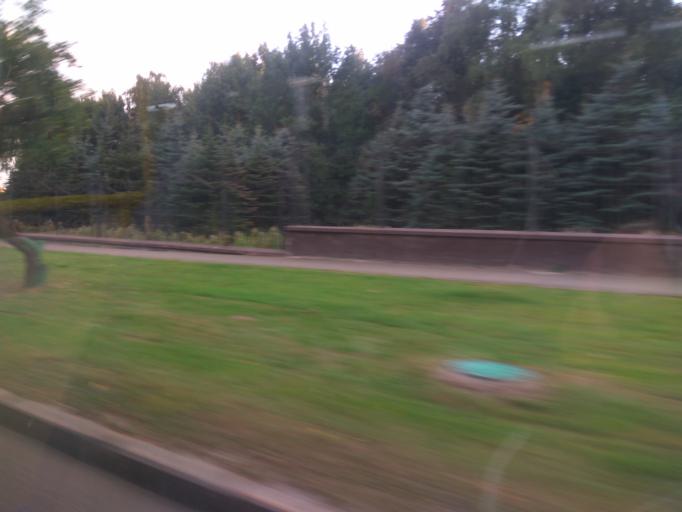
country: RU
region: Moscow
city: Novovladykino
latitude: 55.8387
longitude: 37.5896
